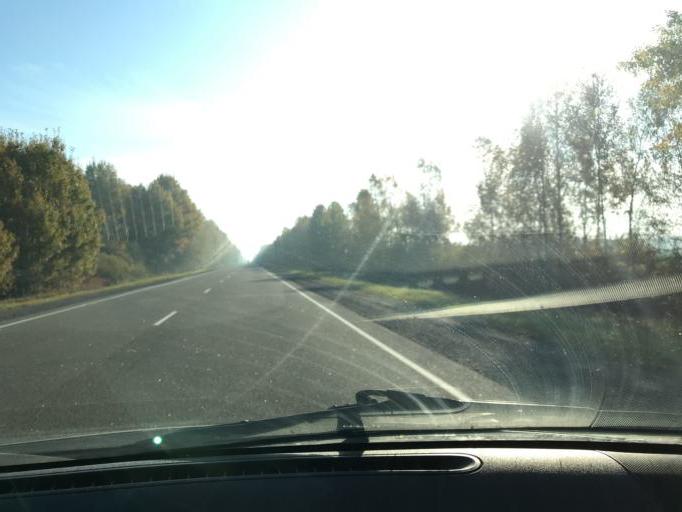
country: BY
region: Brest
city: Horad Luninyets
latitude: 52.3033
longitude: 26.7083
